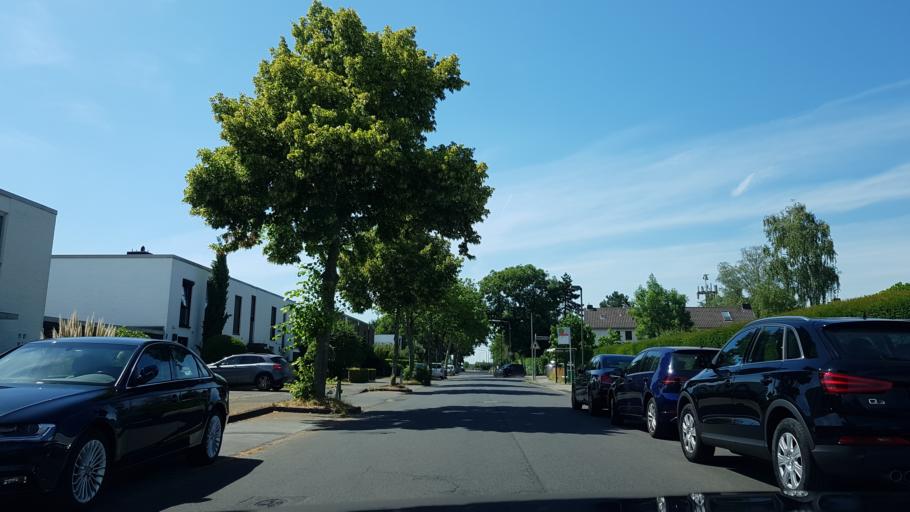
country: DE
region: North Rhine-Westphalia
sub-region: Regierungsbezirk Dusseldorf
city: Meerbusch
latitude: 51.2785
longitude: 6.7273
